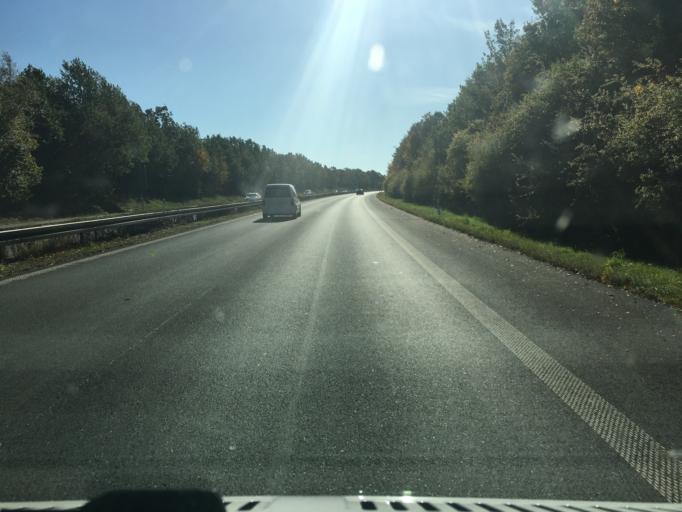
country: DE
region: Saxony
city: Dennheritz
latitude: 50.8051
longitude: 12.4547
